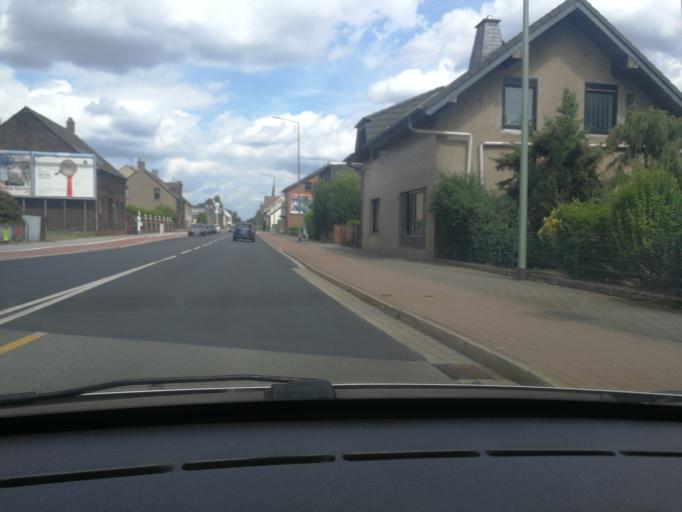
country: DE
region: North Rhine-Westphalia
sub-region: Regierungsbezirk Dusseldorf
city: Moers
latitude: 51.3843
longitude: 6.6538
